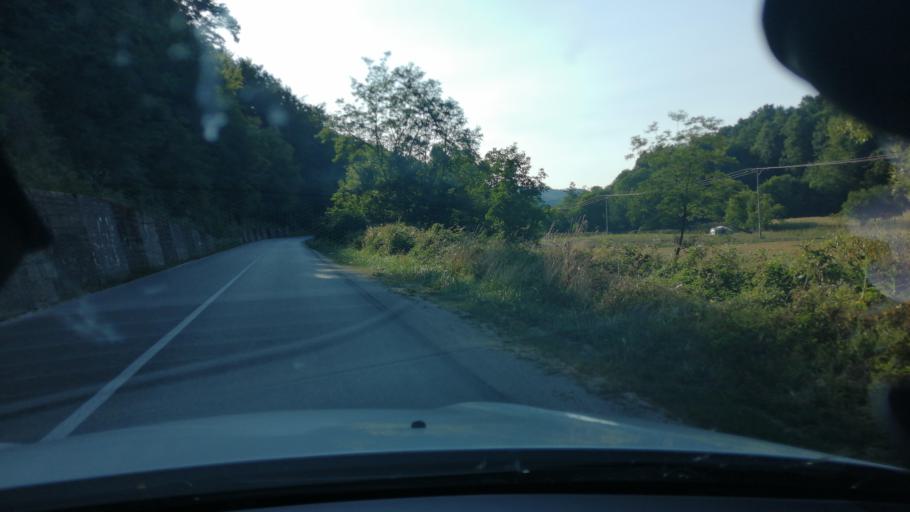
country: RS
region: Central Serbia
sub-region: Moravicki Okrug
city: Ivanjica
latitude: 43.6769
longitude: 20.2571
